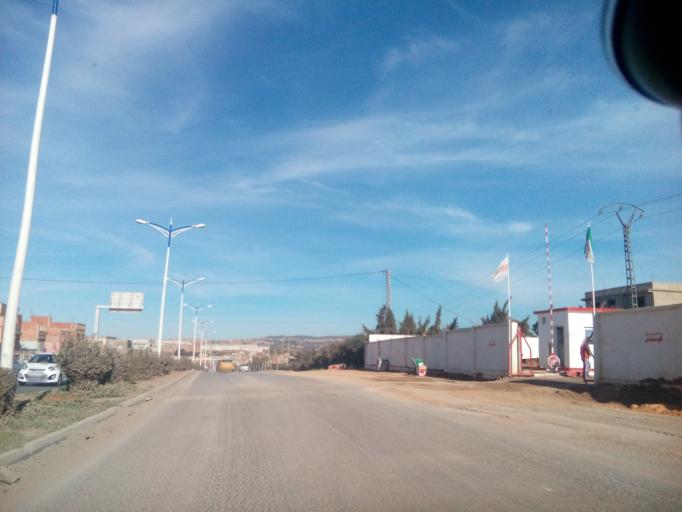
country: DZ
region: Mostaganem
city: Mostaganem
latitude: 35.9328
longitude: 0.1196
